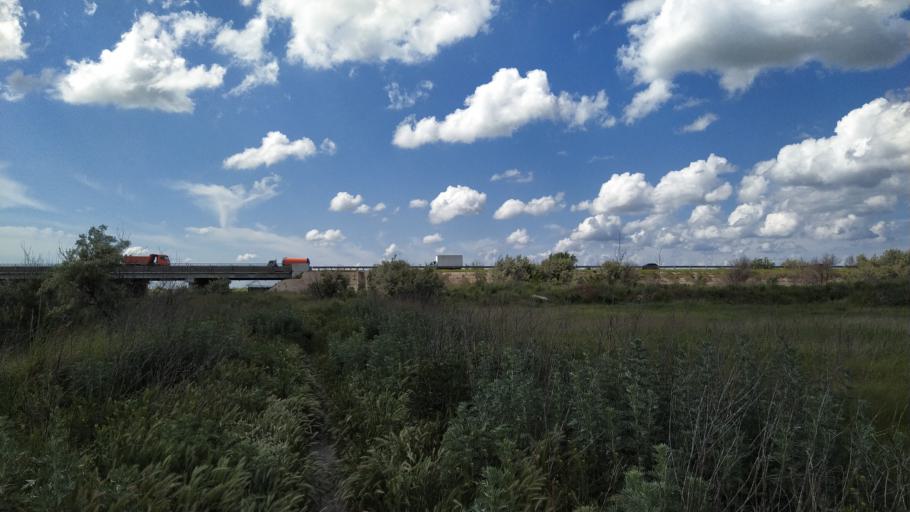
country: RU
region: Rostov
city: Bataysk
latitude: 47.1335
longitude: 39.6780
